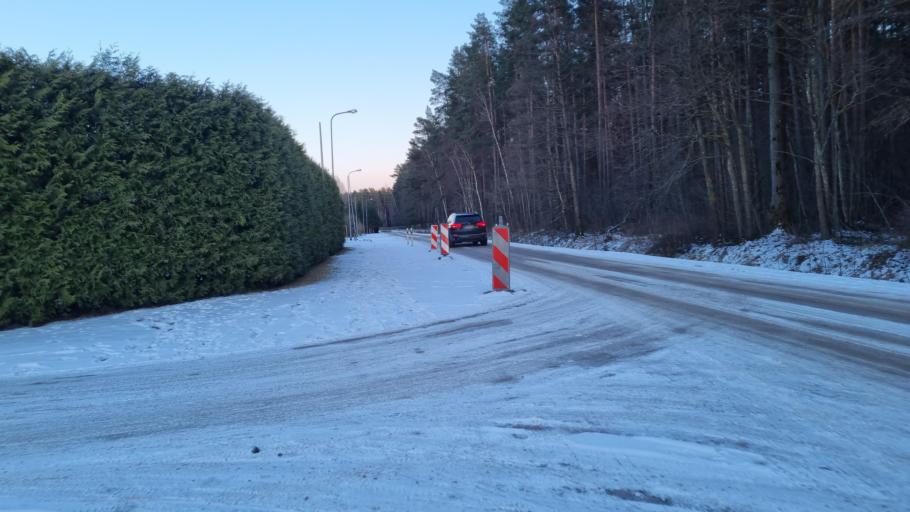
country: LV
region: Babite
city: Pinki
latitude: 56.9663
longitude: 23.9414
